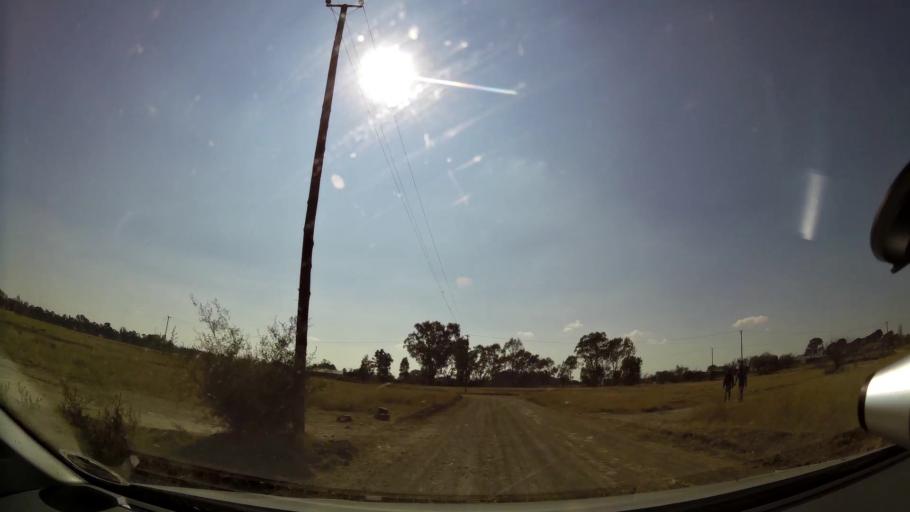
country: ZA
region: Orange Free State
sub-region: Mangaung Metropolitan Municipality
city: Bloemfontein
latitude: -29.1598
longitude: 26.3125
